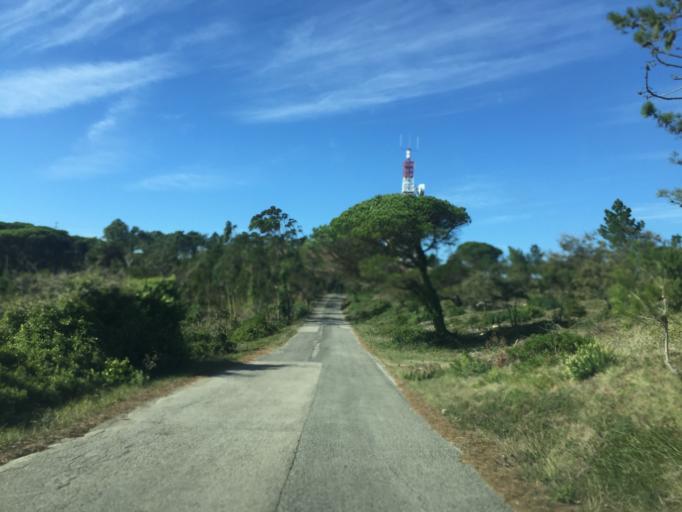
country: PT
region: Coimbra
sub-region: Figueira da Foz
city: Tavarede
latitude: 40.1966
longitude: -8.8588
